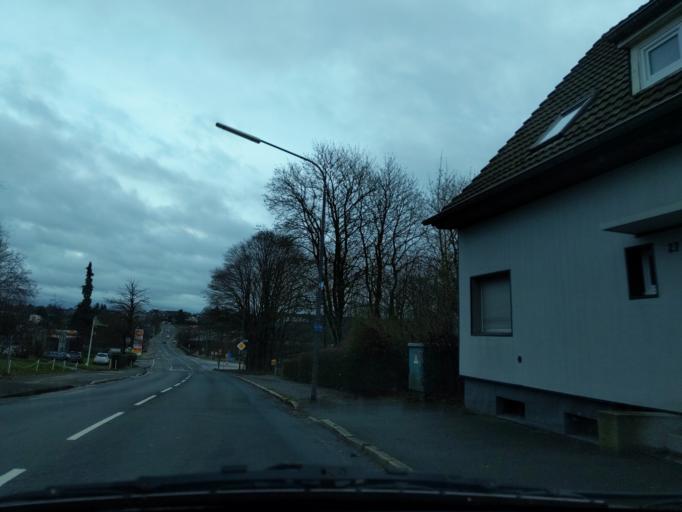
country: DE
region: North Rhine-Westphalia
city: Wermelskirchen
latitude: 51.1384
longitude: 7.1876
